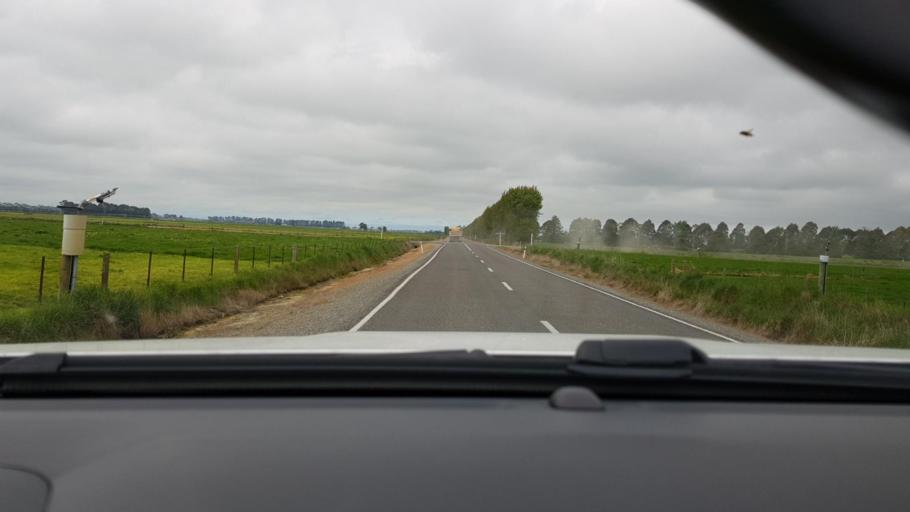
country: NZ
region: Otago
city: Oamaru
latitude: -44.9649
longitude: 170.9370
